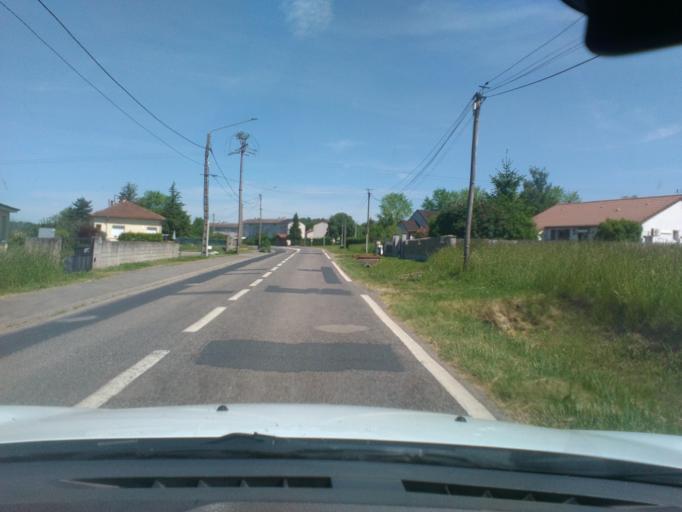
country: FR
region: Lorraine
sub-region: Departement de Meurthe-et-Moselle
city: Gerbeviller
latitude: 48.4481
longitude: 6.5638
